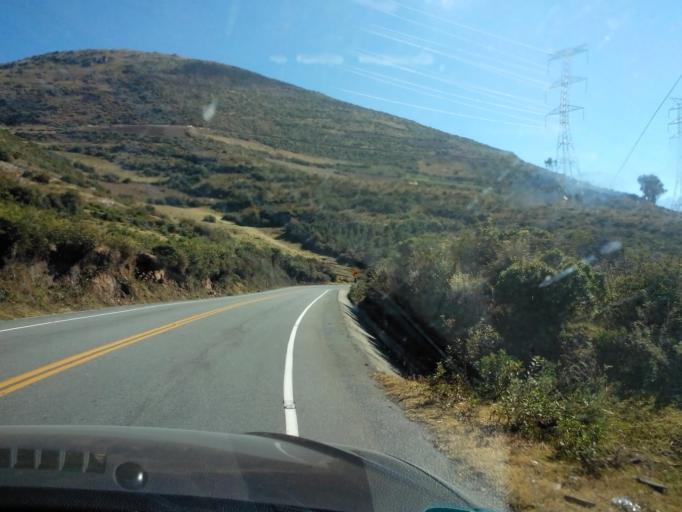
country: PE
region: Apurimac
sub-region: Provincia de Abancay
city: Cachora
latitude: -13.5488
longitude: -72.8092
